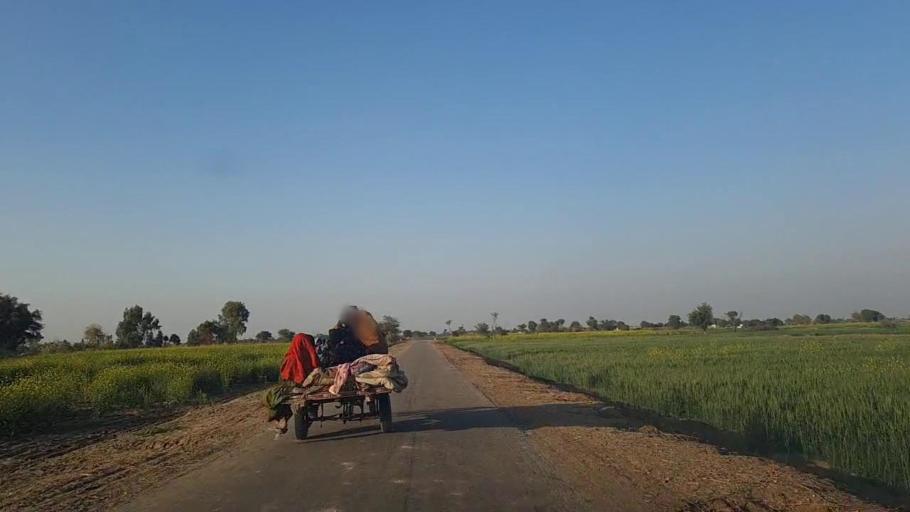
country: PK
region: Sindh
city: Jam Sahib
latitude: 26.3438
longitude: 68.6732
